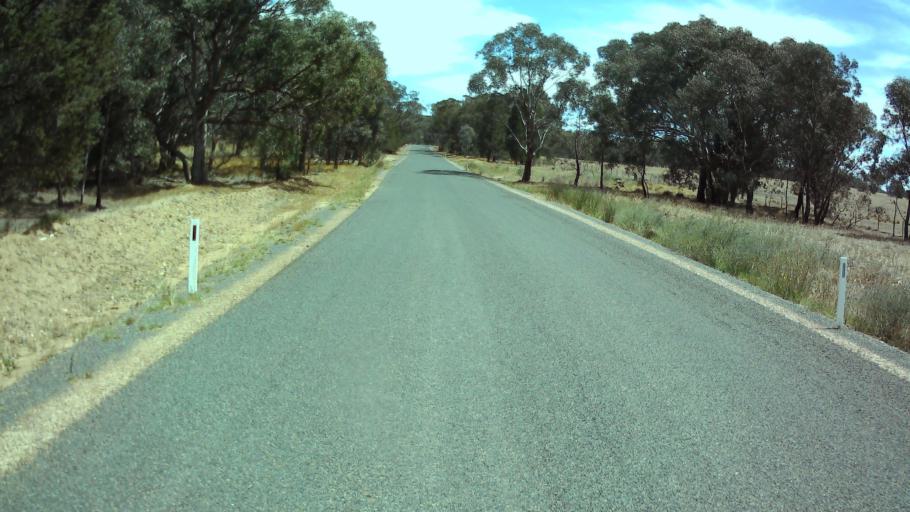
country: AU
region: New South Wales
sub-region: Weddin
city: Grenfell
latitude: -33.7713
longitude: 148.2060
